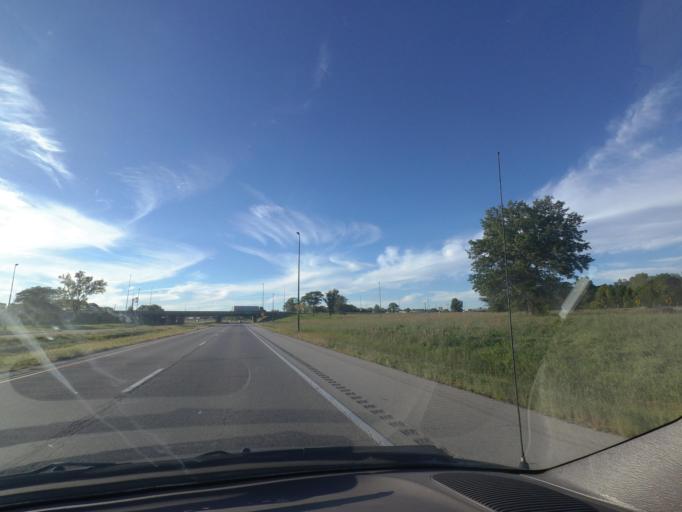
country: US
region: Illinois
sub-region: Sangamon County
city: Grandview
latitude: 39.7851
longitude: -89.5972
